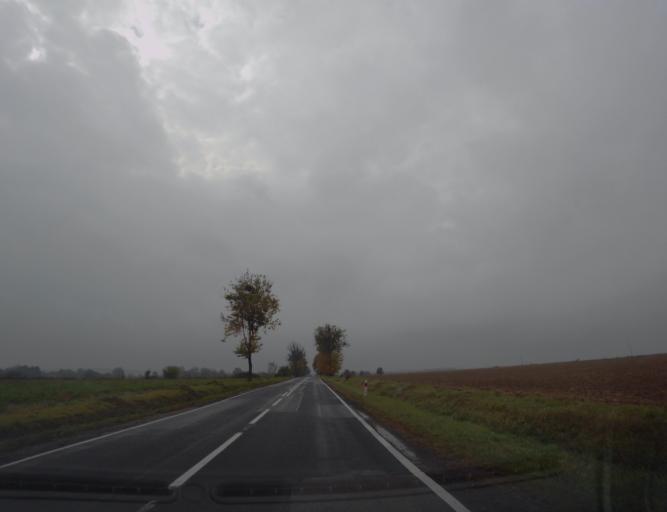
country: PL
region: Lublin Voivodeship
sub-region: Powiat chelmski
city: Rejowiec
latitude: 51.0403
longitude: 23.2502
